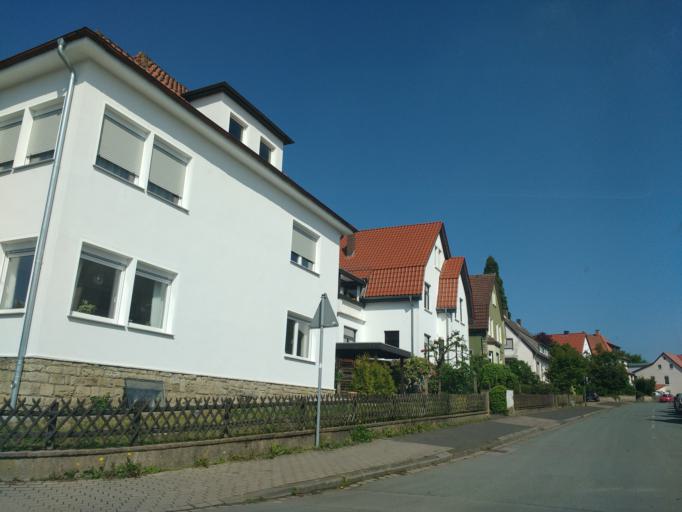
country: DE
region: North Rhine-Westphalia
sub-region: Regierungsbezirk Detmold
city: Lemgo
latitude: 52.0303
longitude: 8.8935
